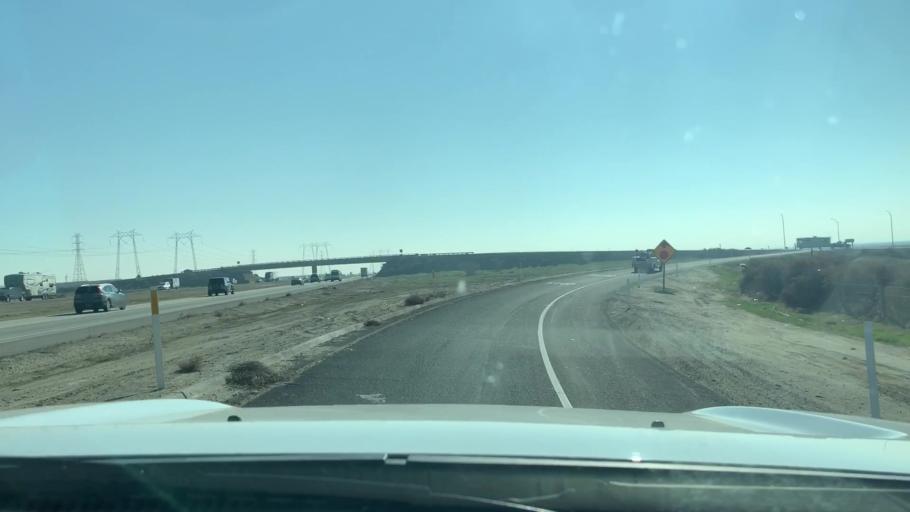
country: US
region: California
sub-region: Kern County
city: Buttonwillow
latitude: 35.5022
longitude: -119.5378
